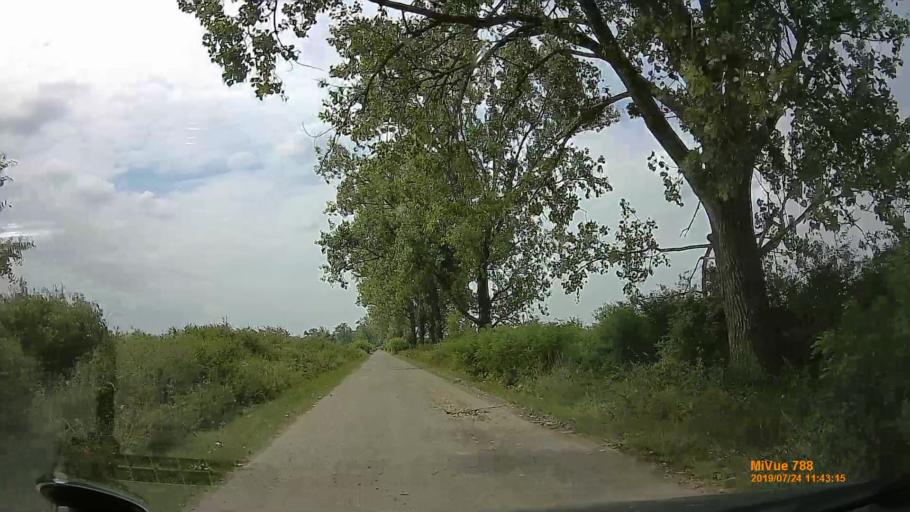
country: UA
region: Zakarpattia
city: Batiovo
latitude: 48.2330
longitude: 22.4529
